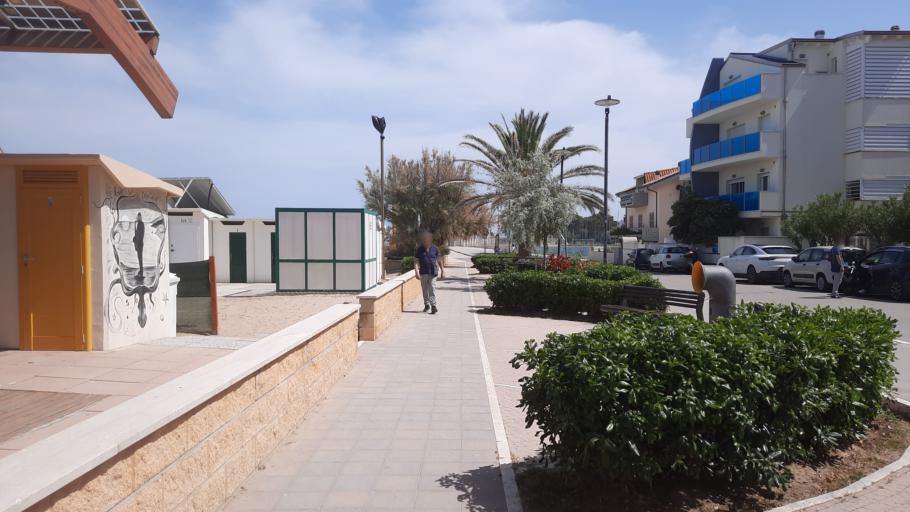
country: IT
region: Abruzzo
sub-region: Provincia di Teramo
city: Pineto
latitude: 42.6130
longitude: 14.0656
